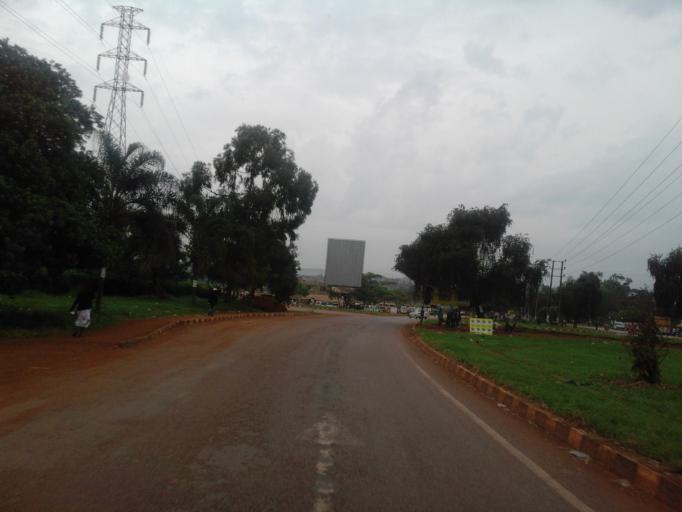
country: UG
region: Central Region
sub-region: Buikwe District
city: Njeru
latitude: 0.4397
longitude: 33.1775
